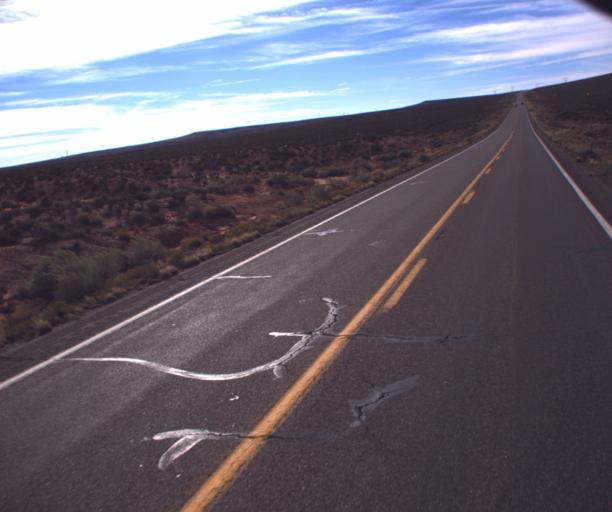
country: US
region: Arizona
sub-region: Coconino County
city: LeChee
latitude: 36.8256
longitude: -111.3093
